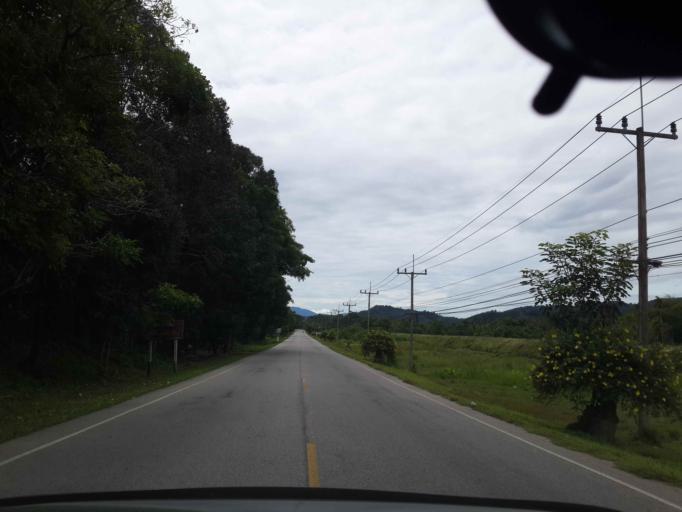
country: TH
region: Narathiwat
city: Yi-ngo
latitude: 6.3501
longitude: 101.6204
